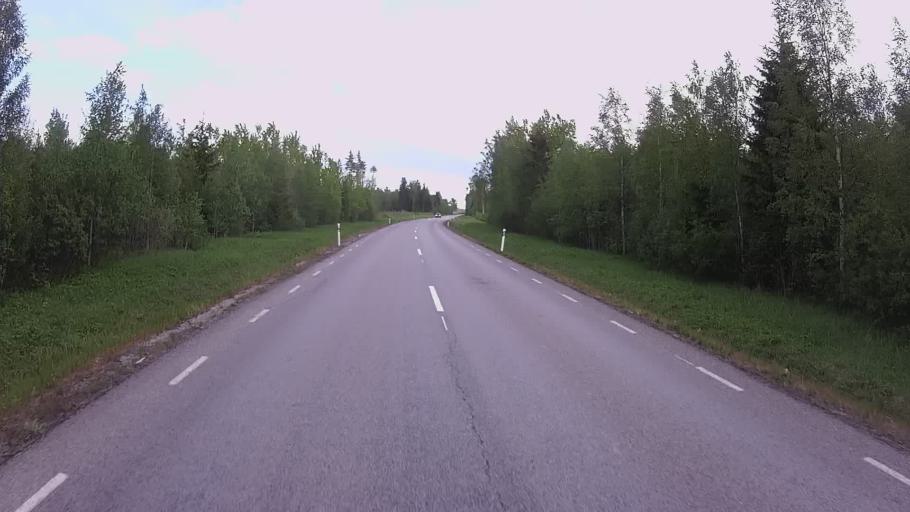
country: EE
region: Jogevamaa
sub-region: Mustvee linn
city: Mustvee
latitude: 59.0809
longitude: 26.9924
